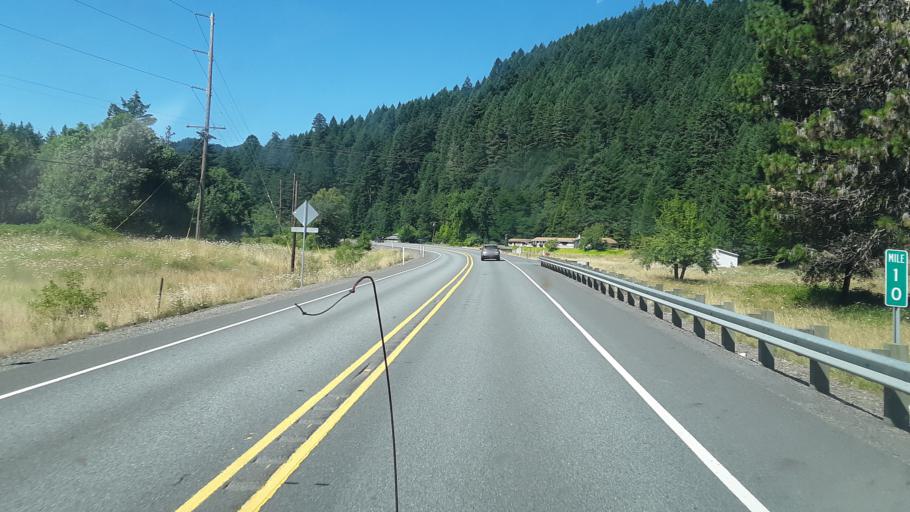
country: US
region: Oregon
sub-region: Josephine County
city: Redwood
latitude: 42.3772
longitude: -123.4965
